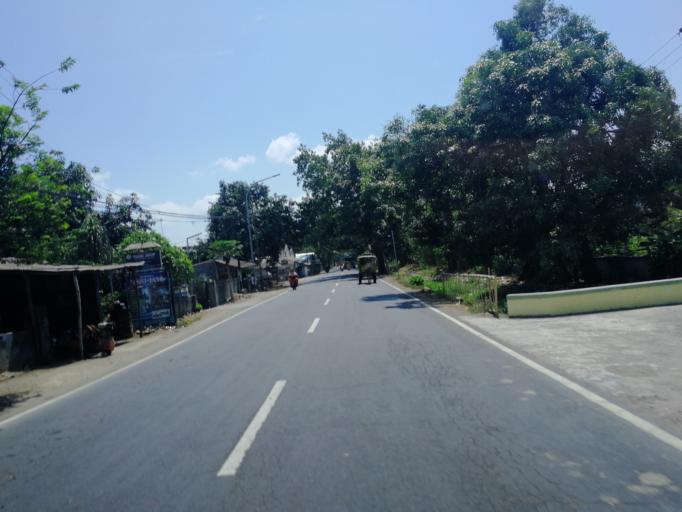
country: ID
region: West Nusa Tenggara
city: Jelateng Timur
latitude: -8.7024
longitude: 116.0956
